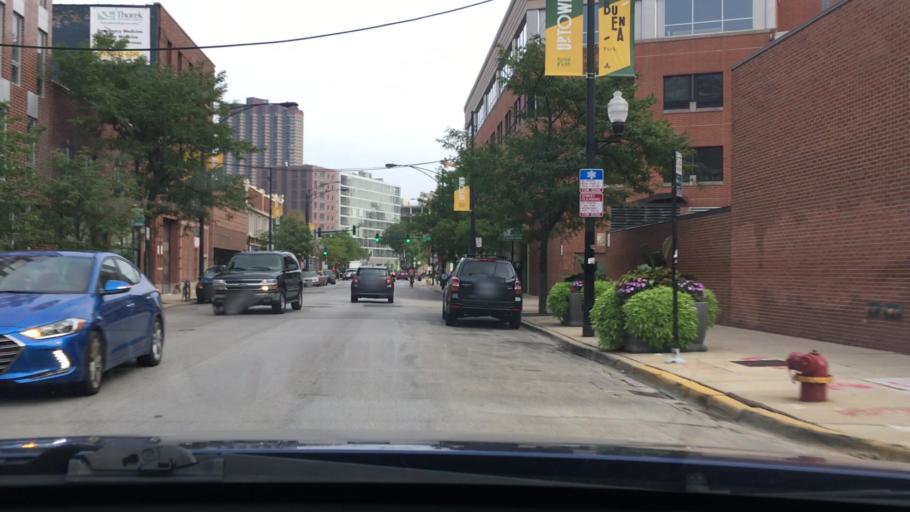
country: US
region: Illinois
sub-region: Cook County
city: Lincolnwood
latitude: 41.9555
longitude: -87.6512
